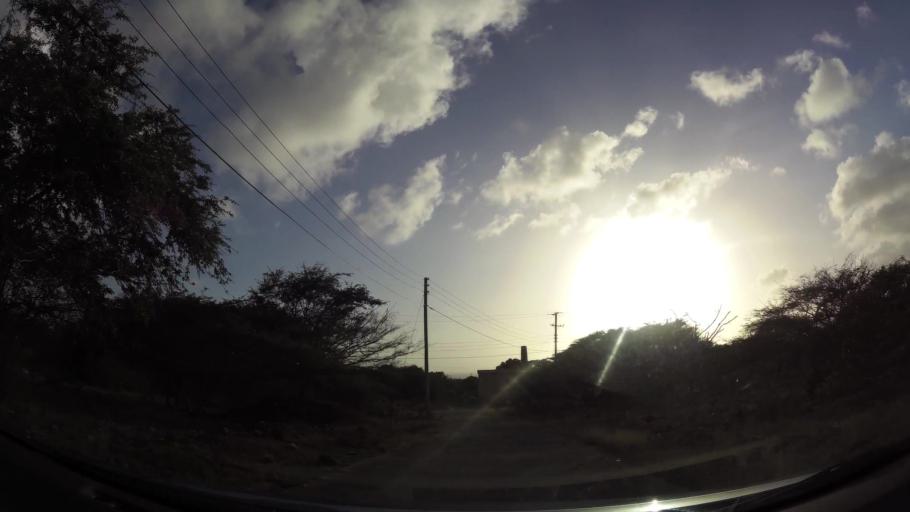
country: KN
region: Saint John Figtree
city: Fig Tree
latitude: 17.1192
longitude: -62.6100
